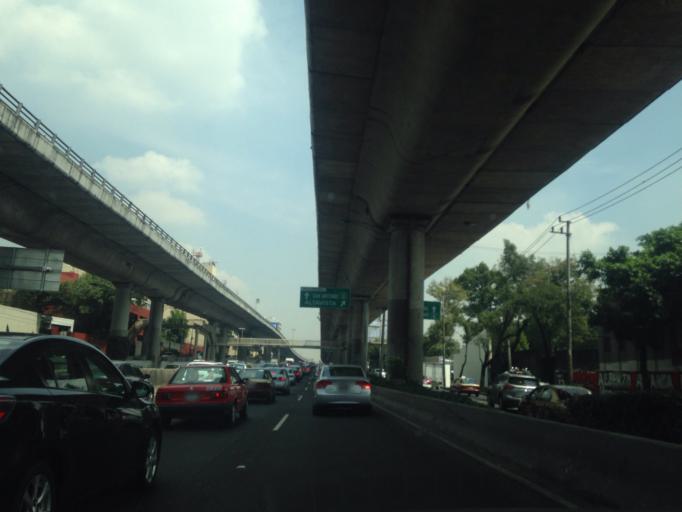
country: MX
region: Mexico City
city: Magdalena Contreras
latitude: 19.3418
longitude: -99.2027
